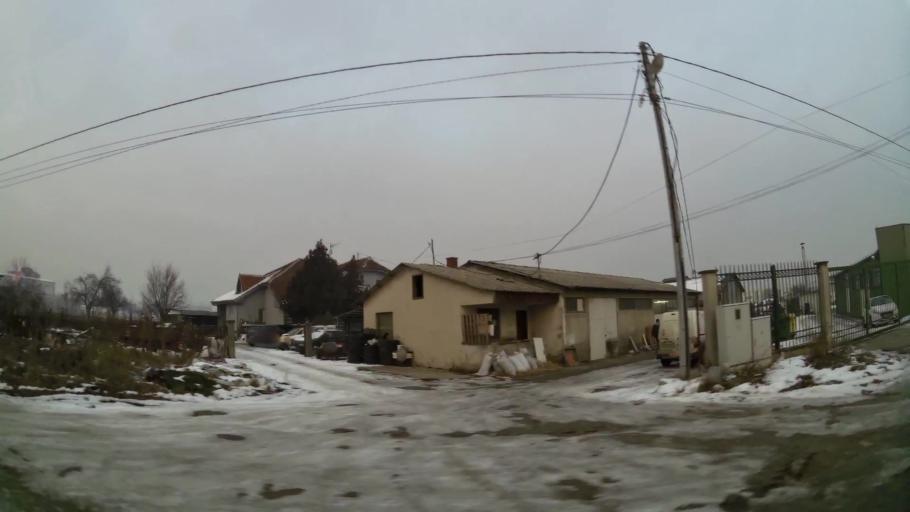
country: MK
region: Suto Orizari
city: Suto Orizare
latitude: 42.0356
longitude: 21.4008
